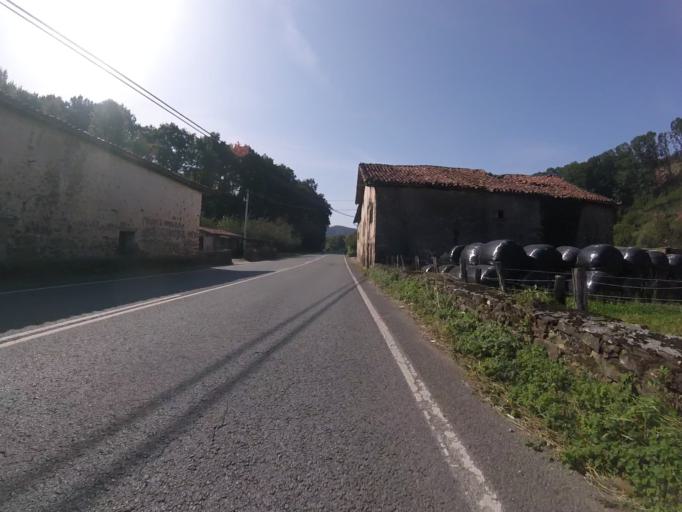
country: ES
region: Navarre
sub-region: Provincia de Navarra
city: Zugarramurdi
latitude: 43.1736
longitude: -1.4933
